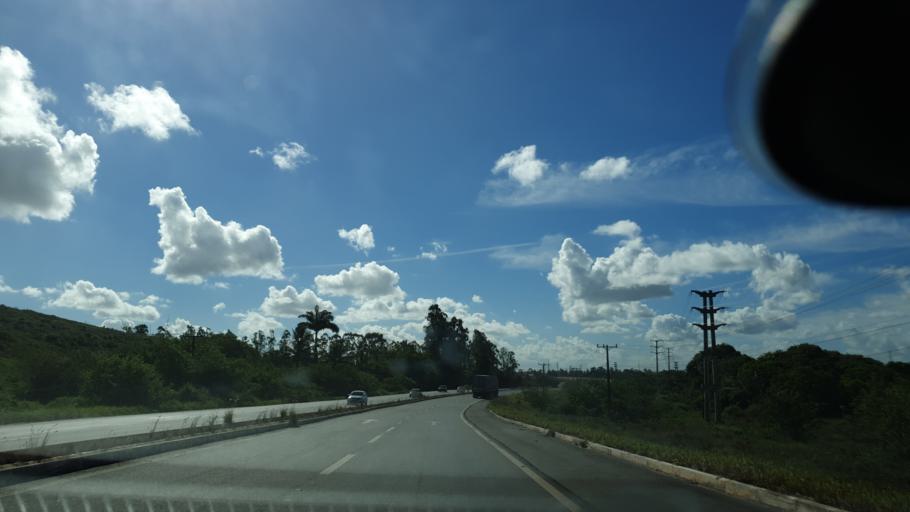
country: BR
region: Bahia
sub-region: Camacari
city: Camacari
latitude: -12.6851
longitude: -38.2597
